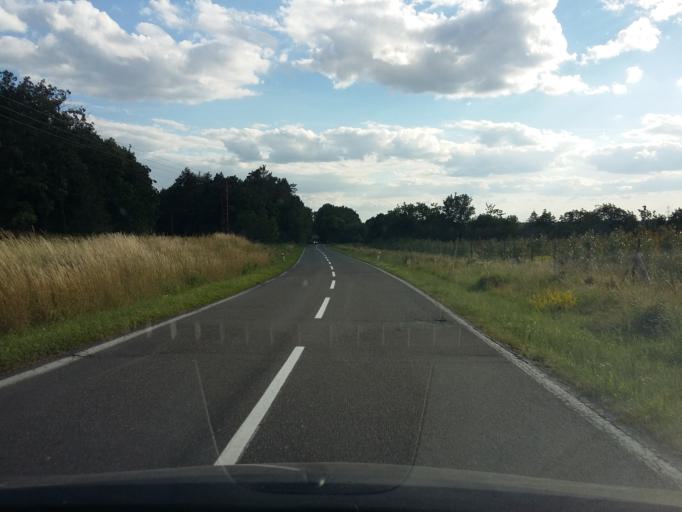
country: SK
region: Trnavsky
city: Smolenice
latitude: 48.5066
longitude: 17.2718
